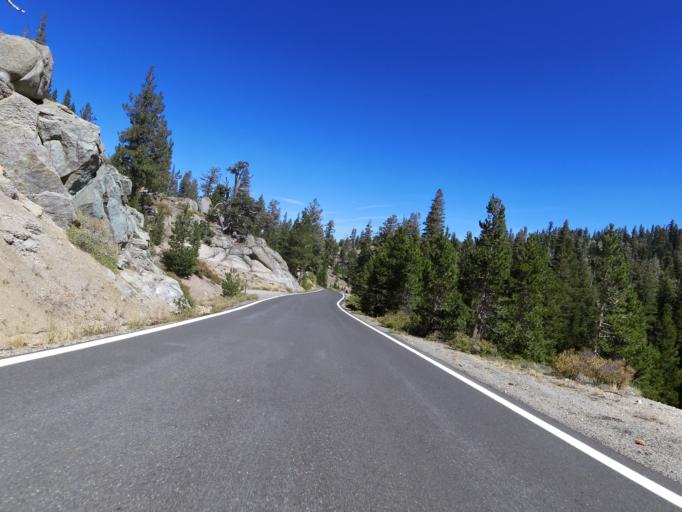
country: US
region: Nevada
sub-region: Douglas County
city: Gardnerville Ranchos
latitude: 38.5633
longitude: -119.8052
